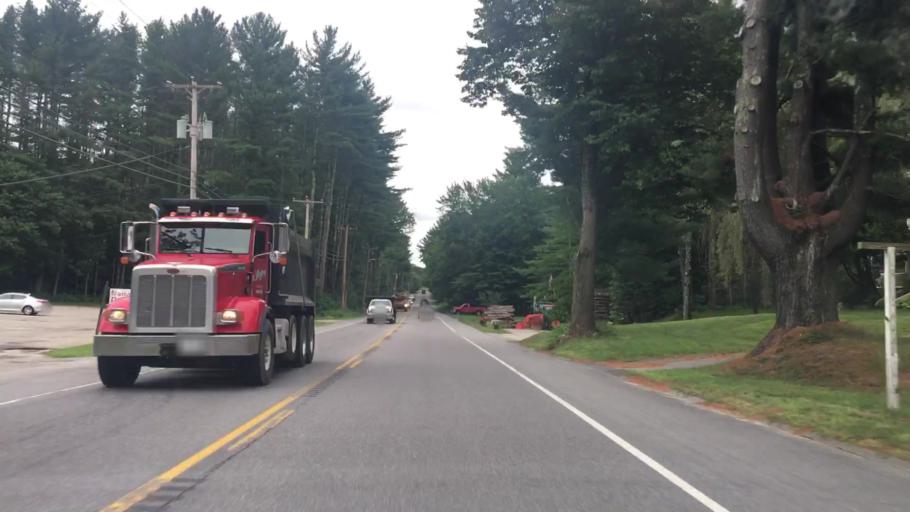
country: US
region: Maine
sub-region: York County
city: Alfred
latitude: 43.4870
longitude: -70.7194
